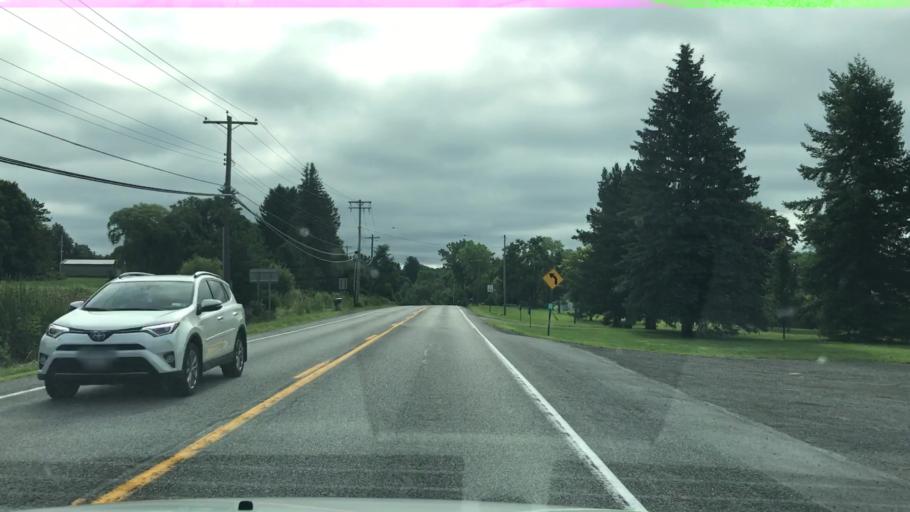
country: US
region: New York
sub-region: Wyoming County
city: Attica
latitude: 42.8363
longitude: -78.3922
